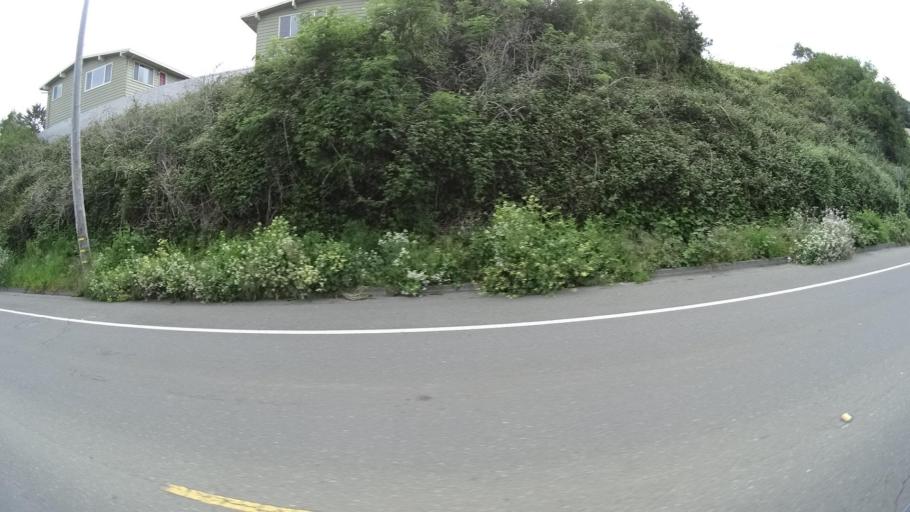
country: US
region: California
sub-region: Humboldt County
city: Arcata
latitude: 40.8805
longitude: -124.0919
